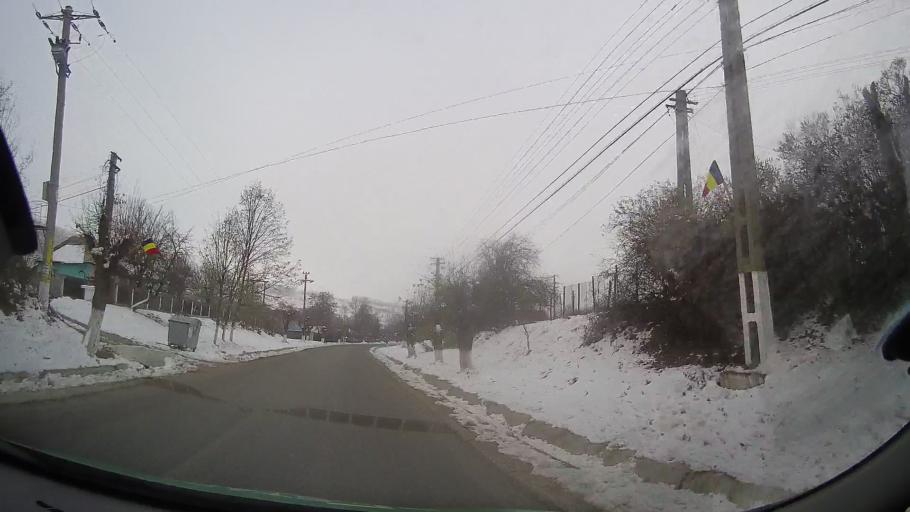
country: RO
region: Bacau
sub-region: Comuna Glavanesti
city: Frumuselu
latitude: 46.2973
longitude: 27.2997
